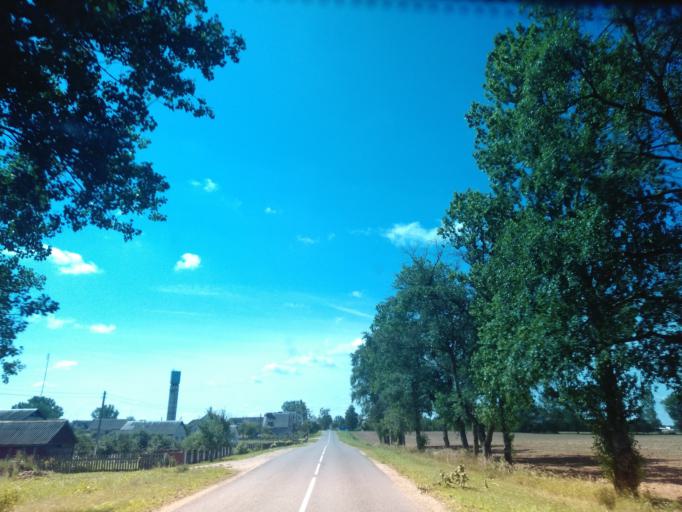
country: BY
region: Minsk
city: Kapyl'
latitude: 53.2621
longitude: 27.1923
